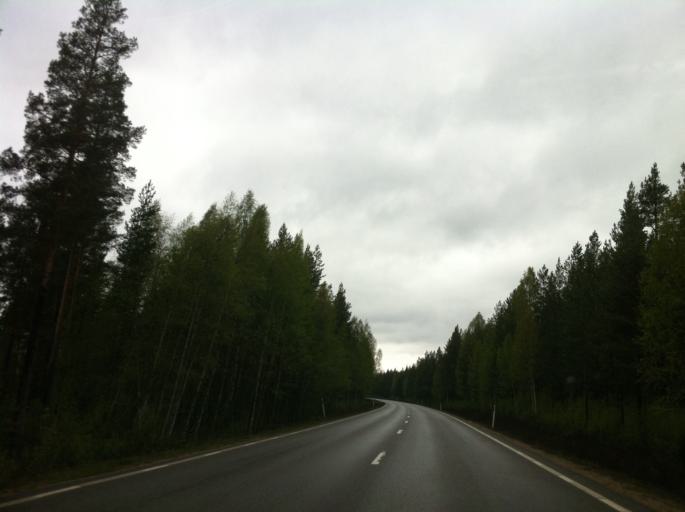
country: SE
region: Jaemtland
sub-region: Harjedalens Kommun
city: Sveg
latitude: 62.1231
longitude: 14.1598
